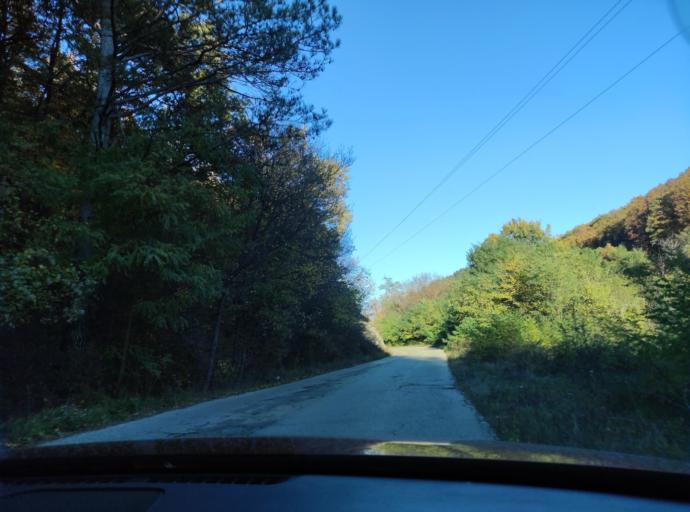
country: BG
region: Montana
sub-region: Obshtina Chiprovtsi
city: Chiprovtsi
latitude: 43.4135
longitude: 22.9420
